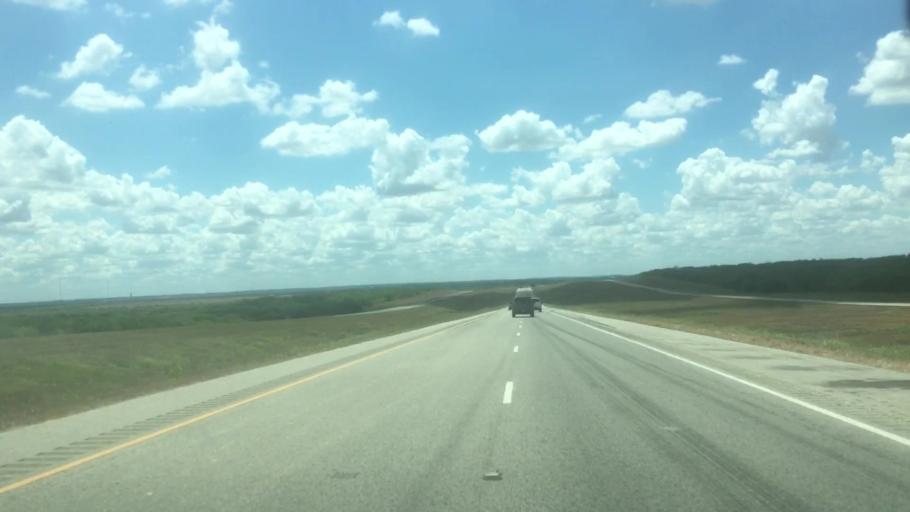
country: US
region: Texas
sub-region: Caldwell County
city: Martindale
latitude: 29.8117
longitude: -97.7664
